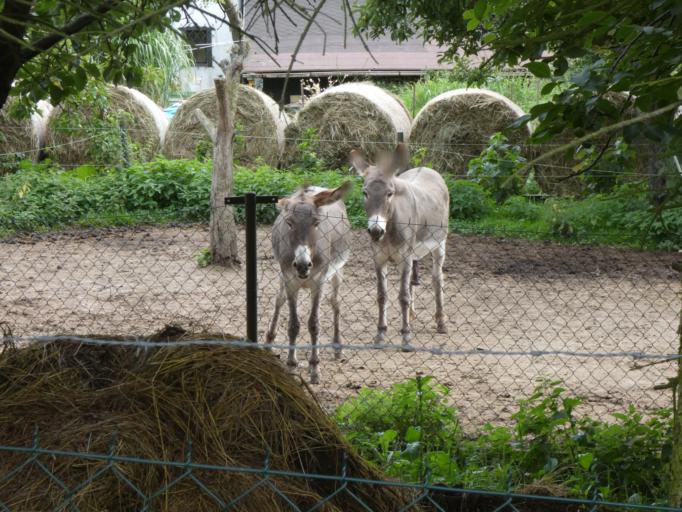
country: CZ
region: Ustecky
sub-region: Okres Decin
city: Decin
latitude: 50.8608
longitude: 14.2673
